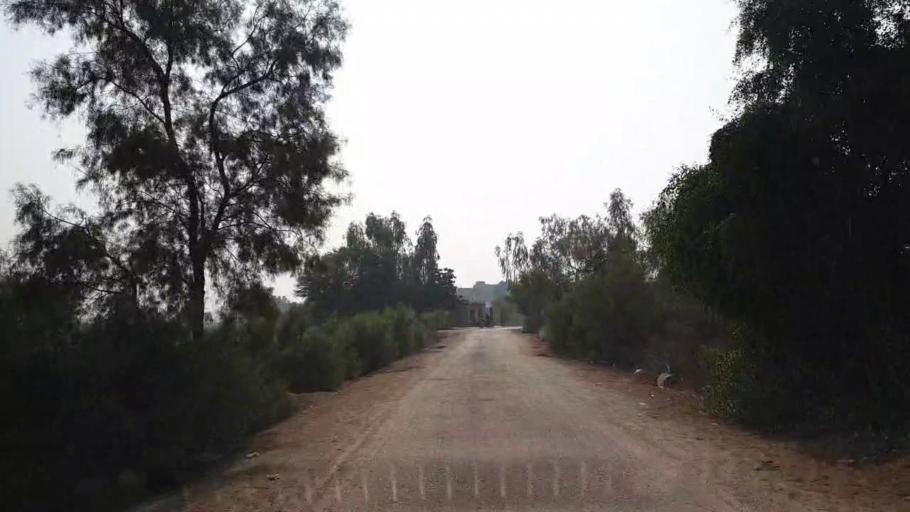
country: PK
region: Sindh
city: Sehwan
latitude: 26.4671
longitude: 67.7775
